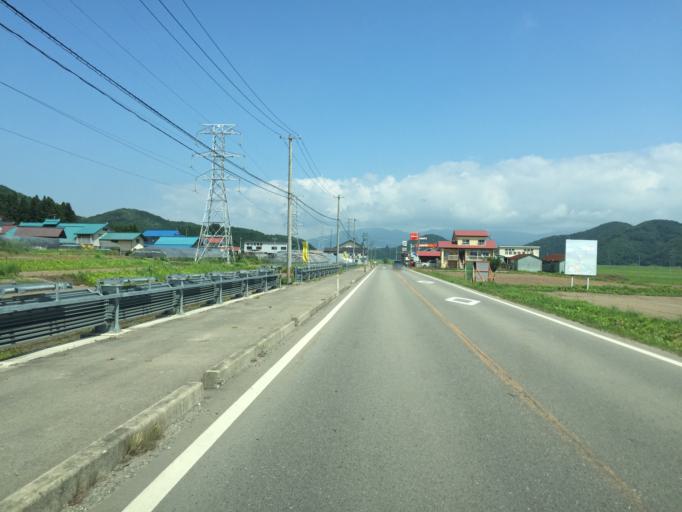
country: JP
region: Fukushima
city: Inawashiro
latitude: 37.4723
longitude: 140.0121
